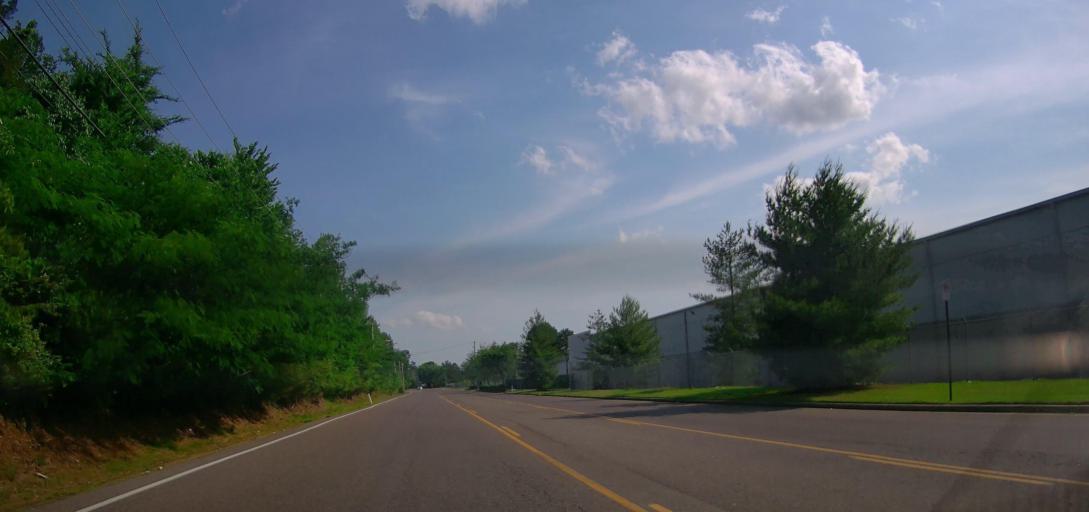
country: US
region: Mississippi
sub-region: De Soto County
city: Olive Branch
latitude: 35.0169
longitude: -89.8488
